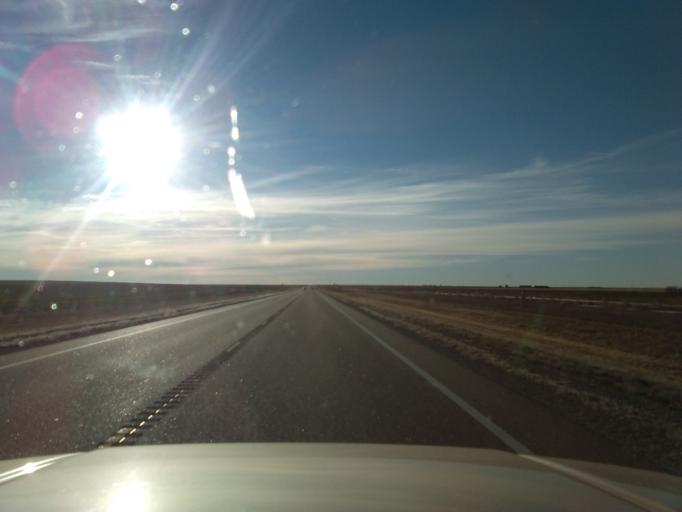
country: US
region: Kansas
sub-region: Sheridan County
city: Hoxie
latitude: 39.5144
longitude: -100.6365
